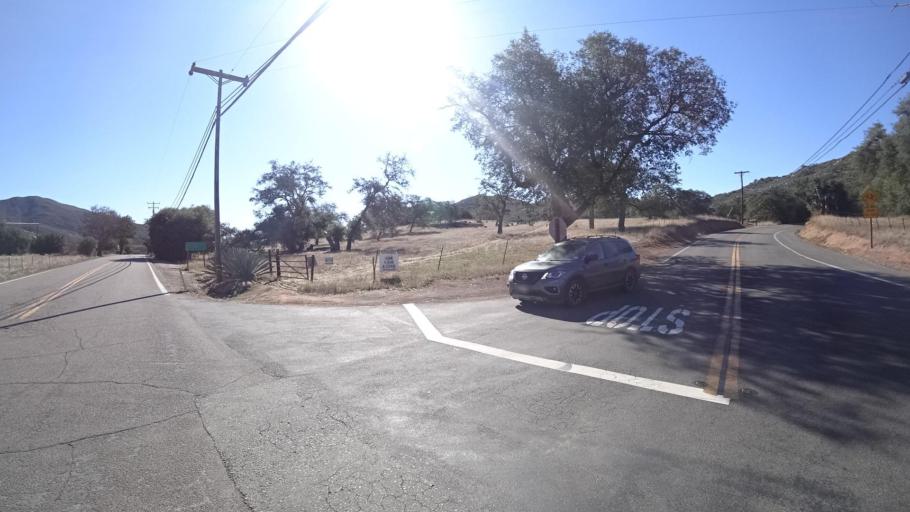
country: US
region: California
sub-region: San Diego County
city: Alpine
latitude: 32.7118
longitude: -116.7470
